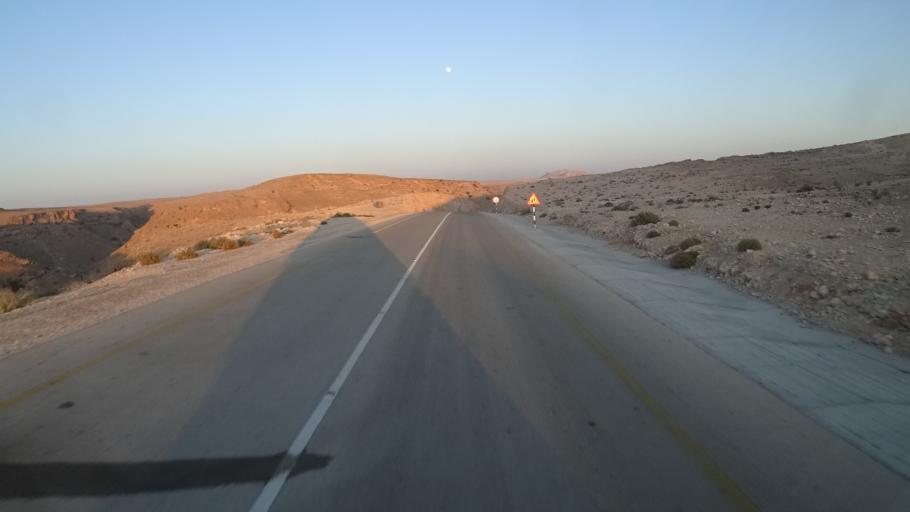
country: YE
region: Al Mahrah
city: Hawf
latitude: 16.9556
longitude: 53.3298
